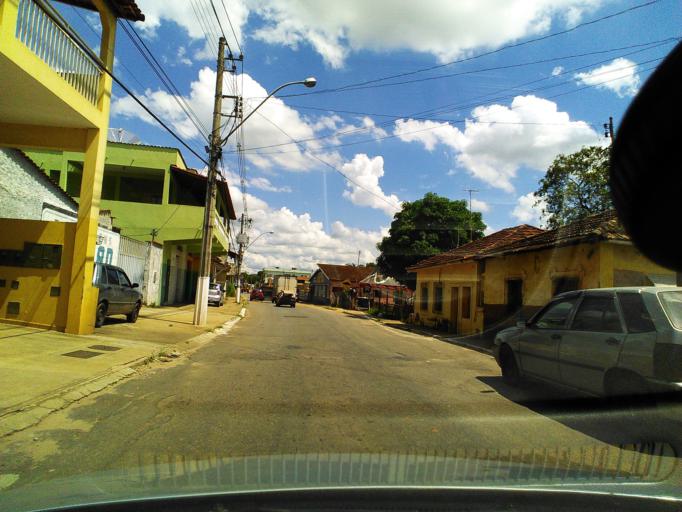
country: BR
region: Minas Gerais
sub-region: Tres Coracoes
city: Tres Coracoes
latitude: -21.7062
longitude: -45.2657
